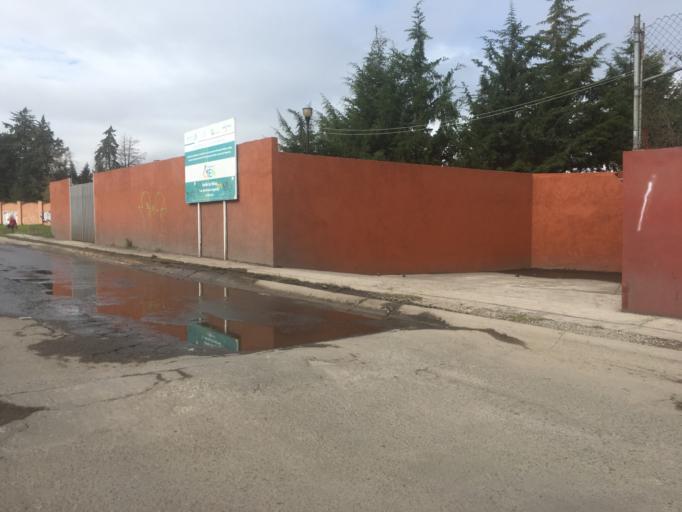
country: MX
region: Mexico
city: Santa Maria Totoltepec
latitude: 19.3011
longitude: -99.5936
